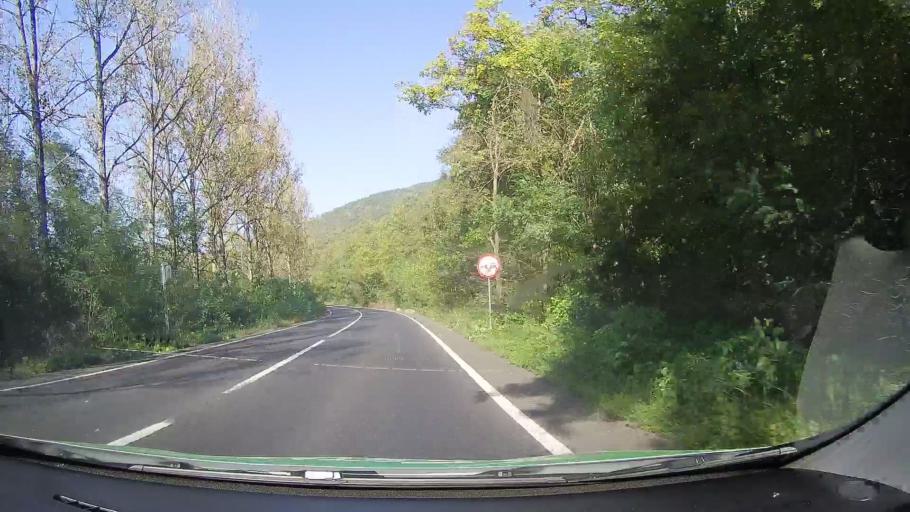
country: RO
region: Arad
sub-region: Comuna Savarsin
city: Savarsin
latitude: 46.0072
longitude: 22.2740
